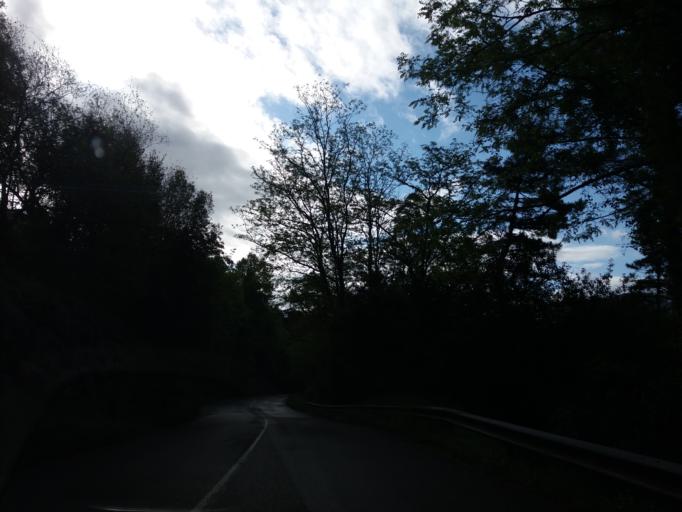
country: ES
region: Cantabria
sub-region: Provincia de Cantabria
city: Ramales de la Victoria
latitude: 43.2676
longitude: -3.4881
